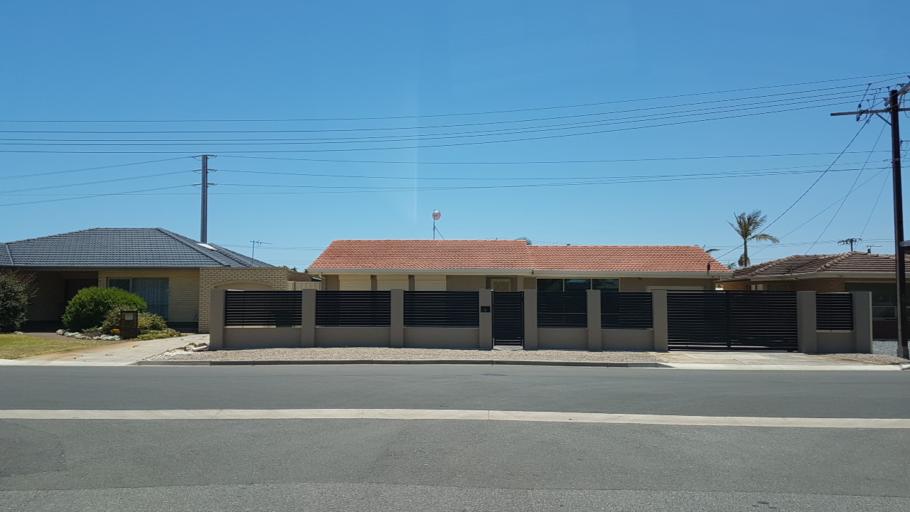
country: AU
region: South Australia
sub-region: Charles Sturt
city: West Lakes Shore
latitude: -34.8575
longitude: 138.4845
